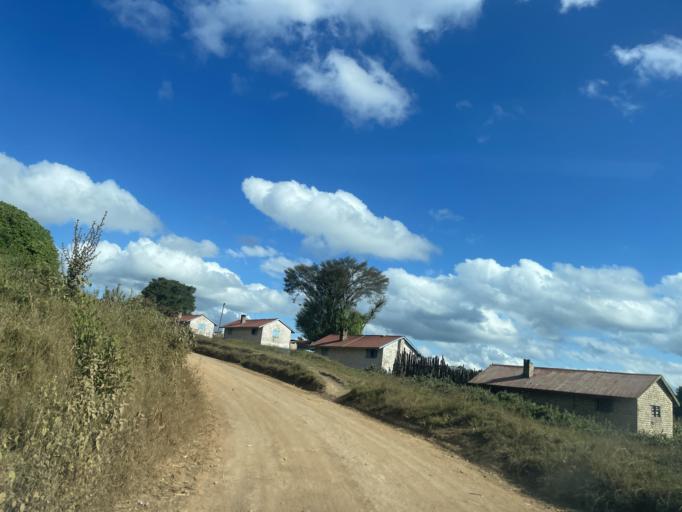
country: TZ
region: Iringa
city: Makungu
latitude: -8.4749
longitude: 35.4185
